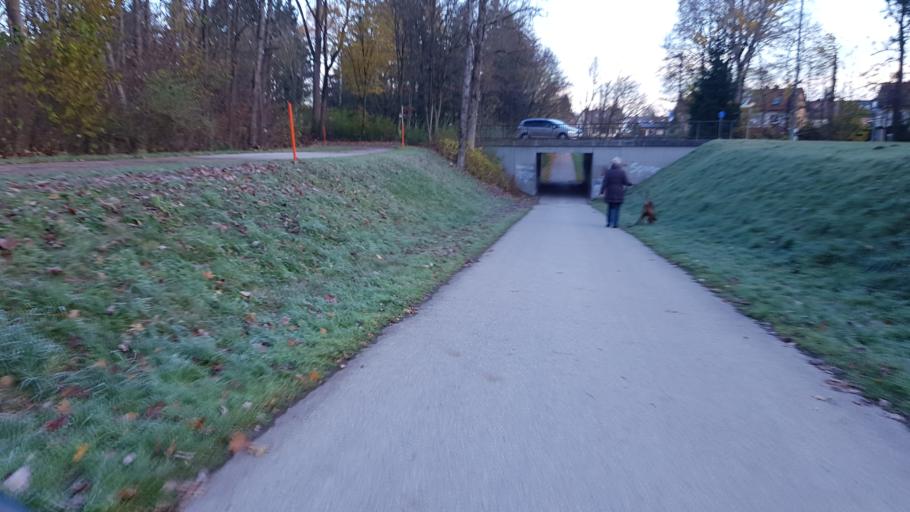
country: DE
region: Bavaria
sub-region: Upper Bavaria
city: Unterhaching
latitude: 48.0784
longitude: 11.5995
